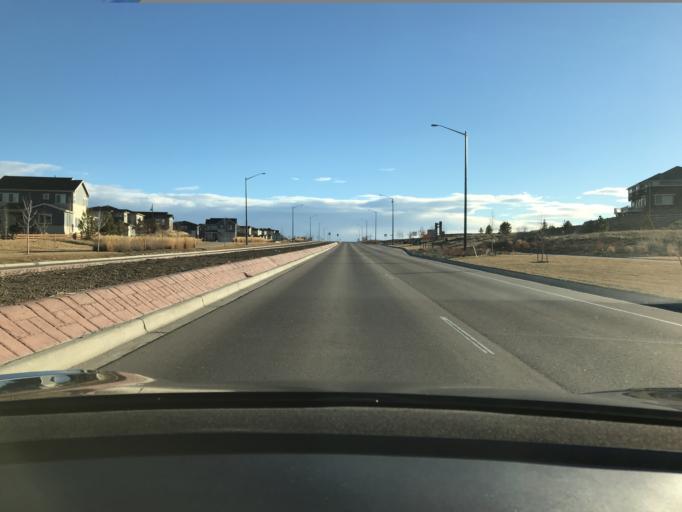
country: US
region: Colorado
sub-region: Boulder County
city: Erie
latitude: 40.0436
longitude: -105.0302
